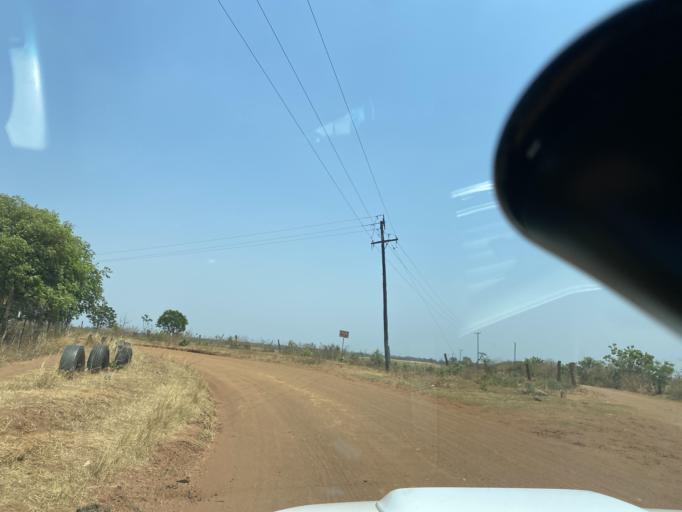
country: ZM
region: Lusaka
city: Lusaka
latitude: -15.4425
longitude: 28.0504
